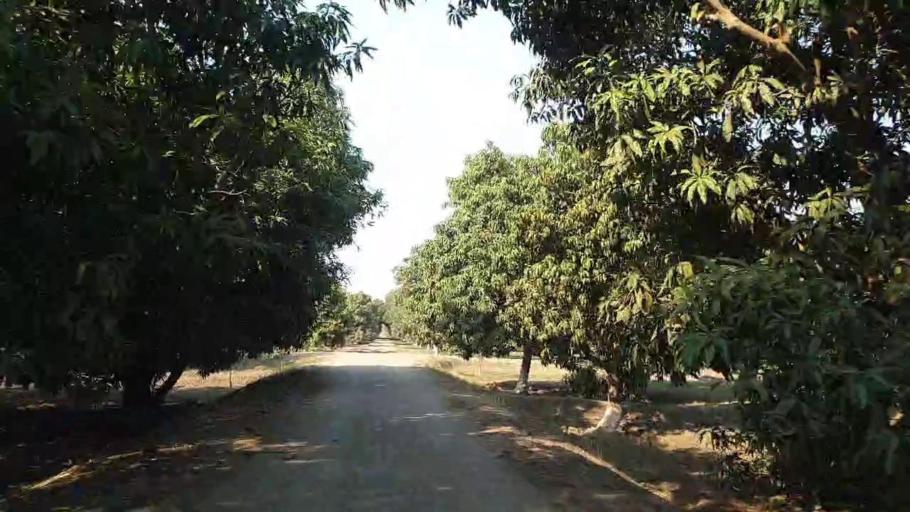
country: PK
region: Sindh
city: Tando Allahyar
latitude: 25.5771
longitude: 68.6722
